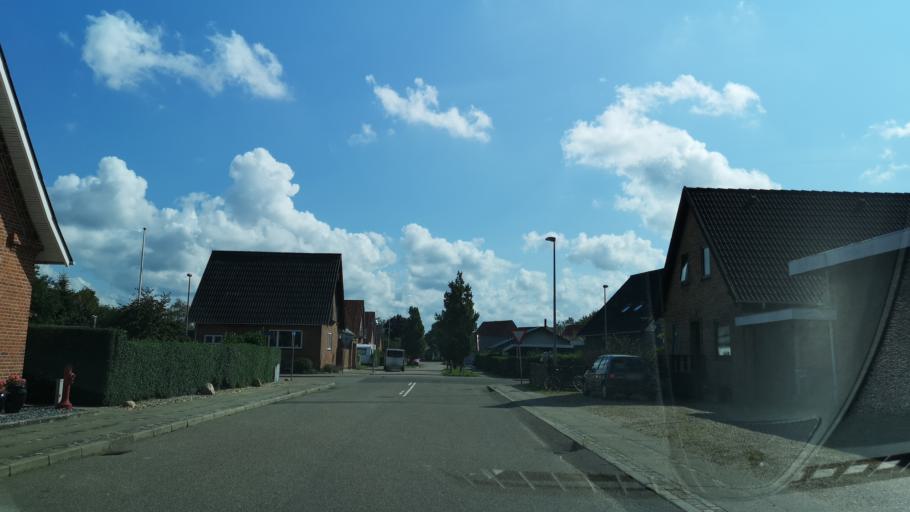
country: DK
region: Central Jutland
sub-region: Ringkobing-Skjern Kommune
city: Skjern
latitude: 55.9504
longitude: 8.4966
